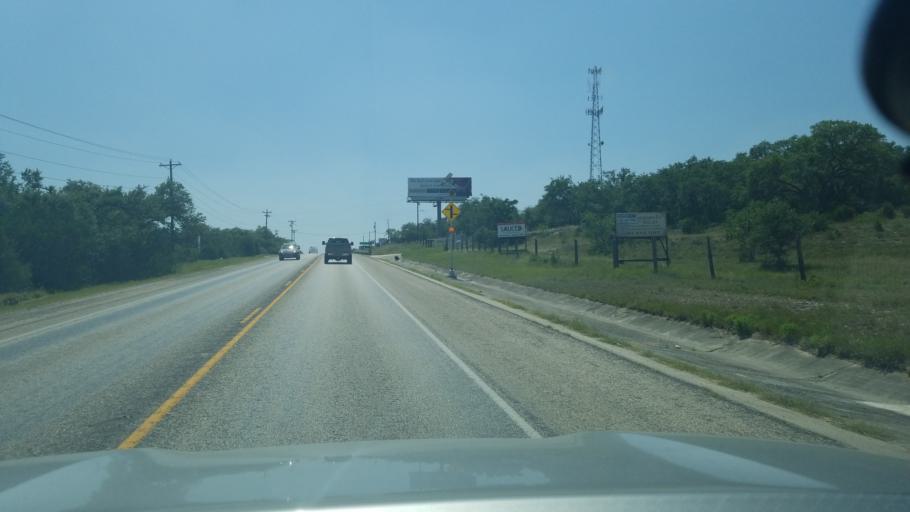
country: US
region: Texas
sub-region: Bexar County
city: Fair Oaks Ranch
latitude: 29.8140
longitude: -98.6257
